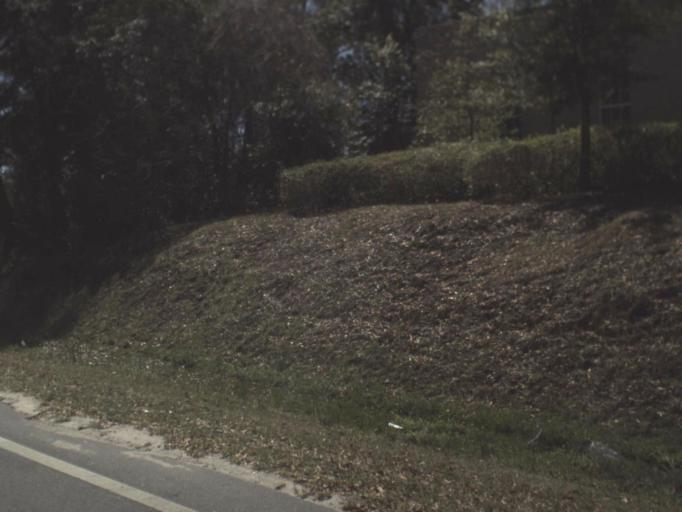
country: US
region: Florida
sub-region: Gadsden County
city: Midway
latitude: 30.5295
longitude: -84.3624
